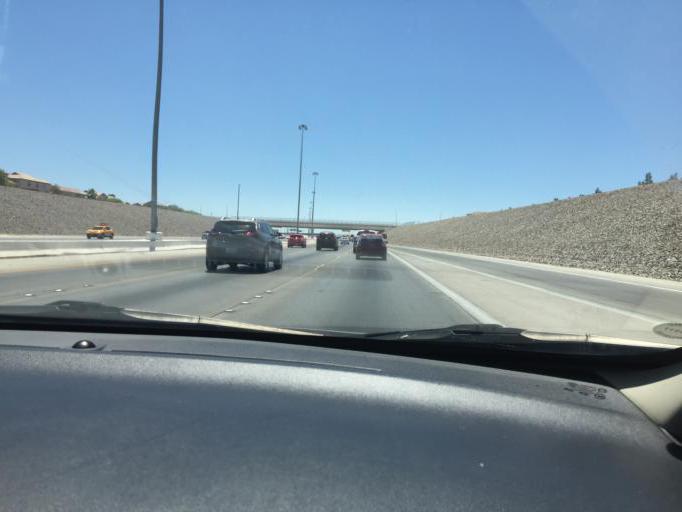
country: US
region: Nevada
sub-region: Clark County
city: Whitney
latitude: 36.0383
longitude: -115.1340
